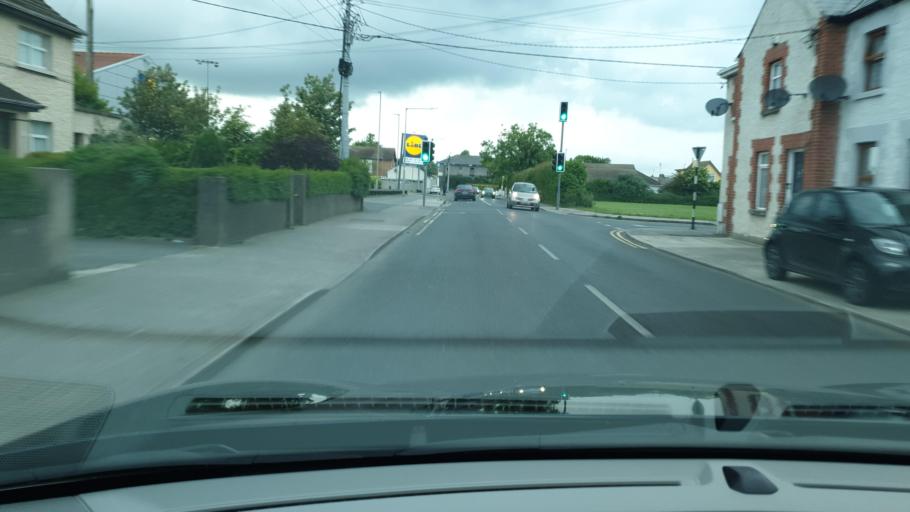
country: IE
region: Leinster
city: Balbriggan
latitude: 53.6060
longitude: -6.1786
